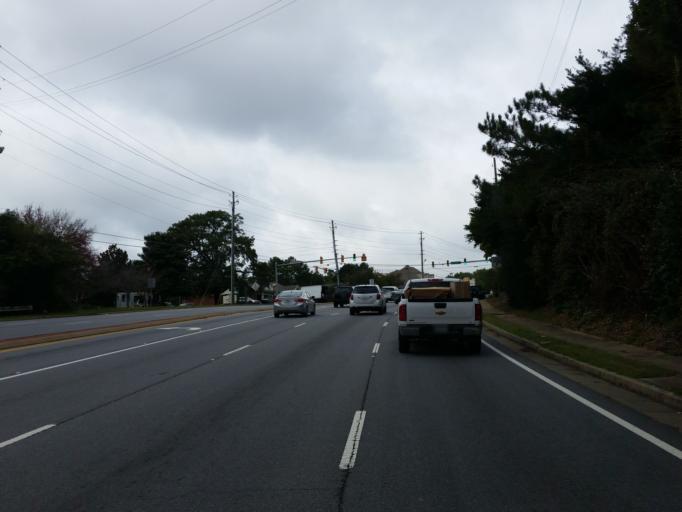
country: US
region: Georgia
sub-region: Fulton County
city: Sandy Springs
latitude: 33.9489
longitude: -84.4107
